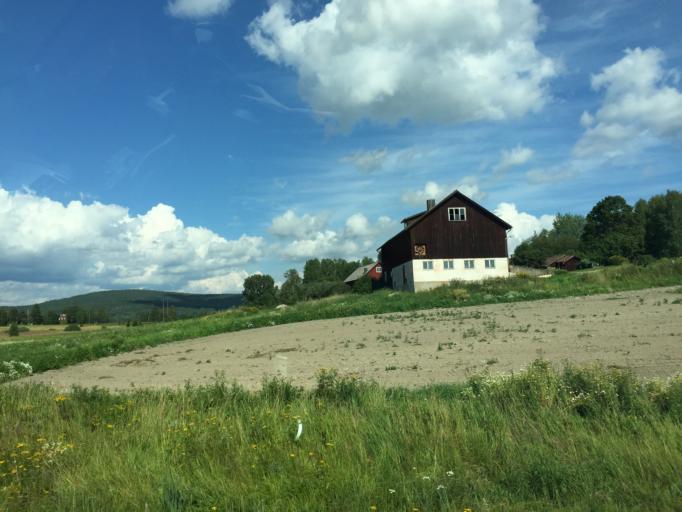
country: SE
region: Gaevleborg
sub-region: Bollnas Kommun
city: Kilafors
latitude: 61.2376
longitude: 16.5524
